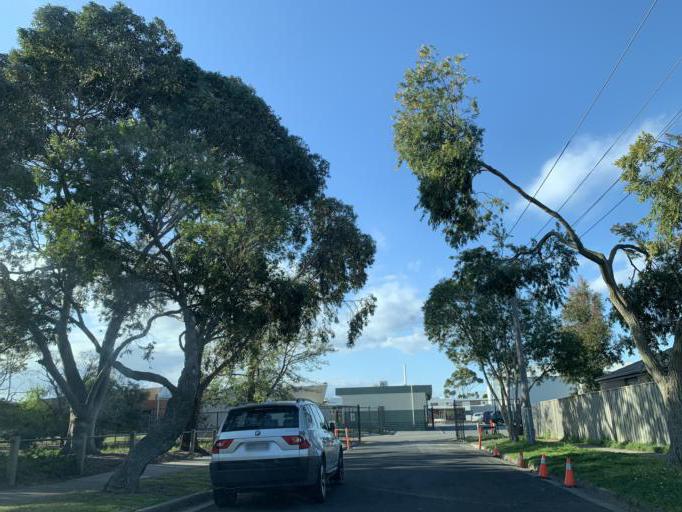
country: AU
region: Victoria
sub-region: Kingston
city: Mordialloc
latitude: -37.9914
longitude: 145.0948
